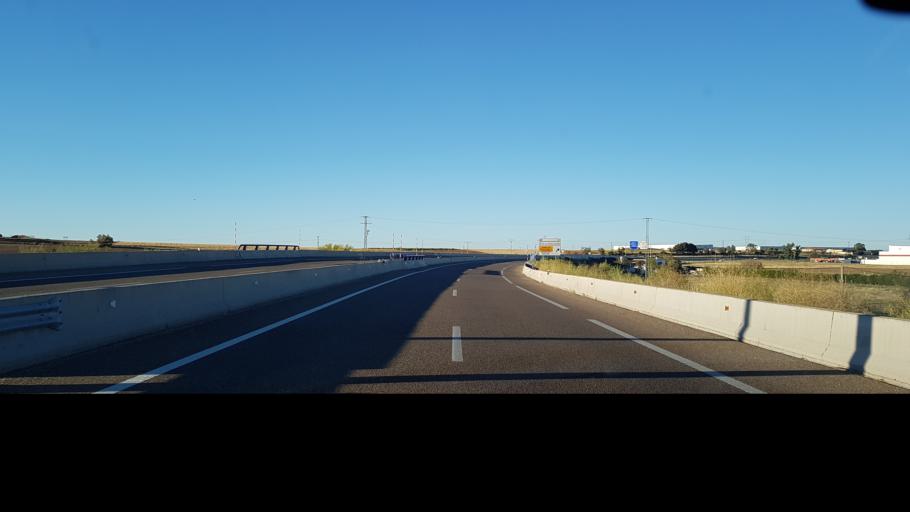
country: ES
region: Castille and Leon
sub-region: Provincia de Zamora
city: Valcabado
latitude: 41.5479
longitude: -5.7576
